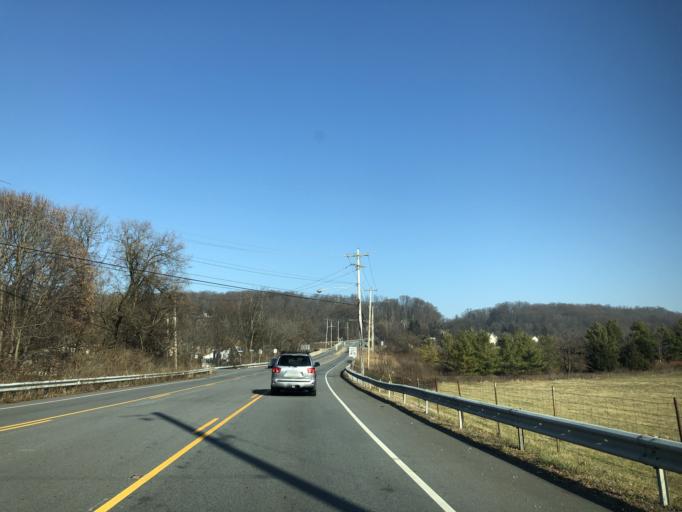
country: US
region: Pennsylvania
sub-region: Chester County
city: Downingtown
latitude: 40.0169
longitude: -75.6951
